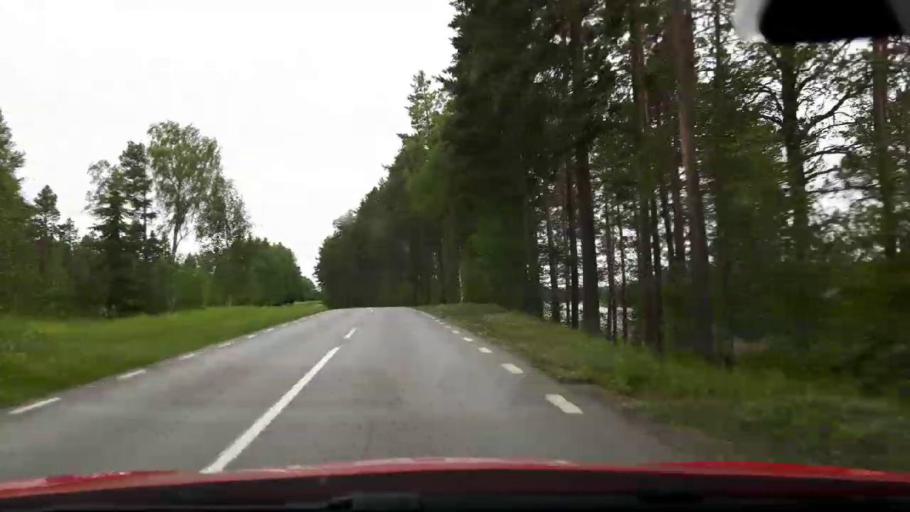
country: SE
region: Jaemtland
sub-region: Stroemsunds Kommun
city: Stroemsund
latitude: 63.4947
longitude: 15.4567
